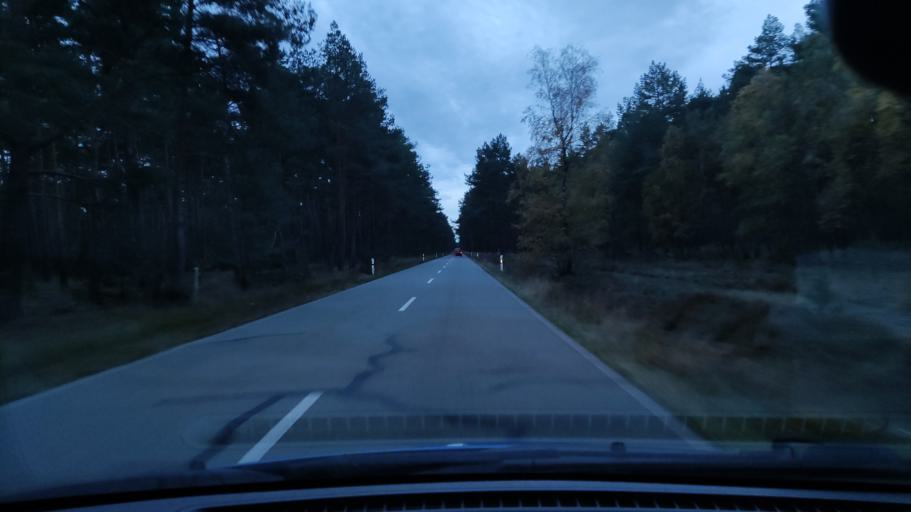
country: DE
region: Lower Saxony
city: Prezelle
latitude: 53.0061
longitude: 11.3908
